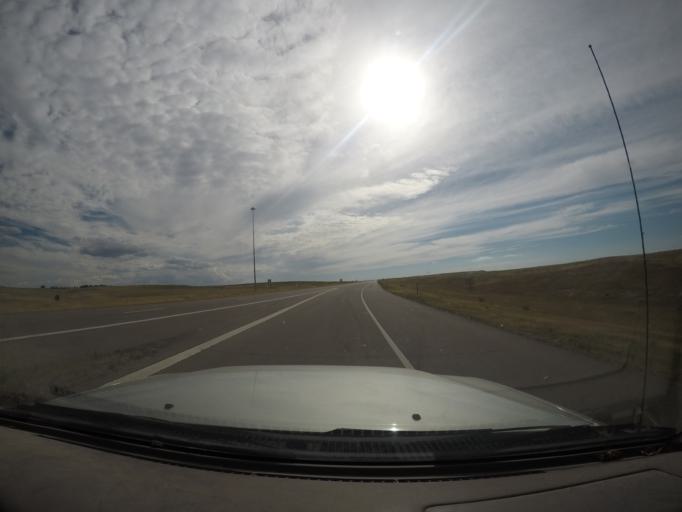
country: US
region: Nebraska
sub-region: Kimball County
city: Kimball
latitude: 41.2160
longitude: -103.6689
